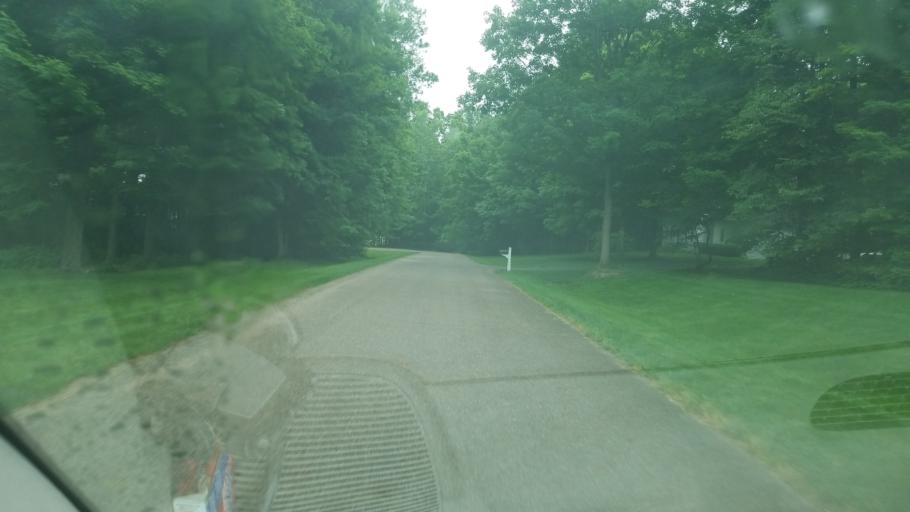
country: US
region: Ohio
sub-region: Knox County
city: Fredericktown
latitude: 40.4915
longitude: -82.5686
